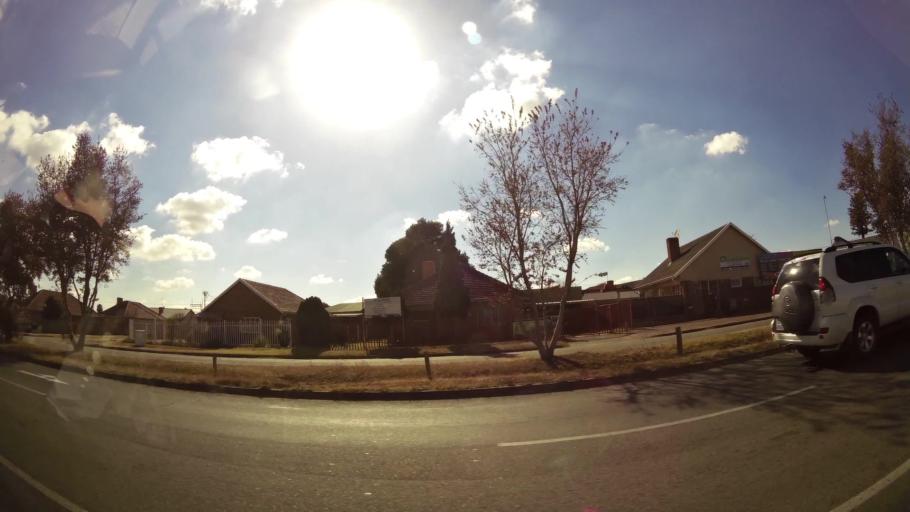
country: ZA
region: Gauteng
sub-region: City of Johannesburg Metropolitan Municipality
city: Roodepoort
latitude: -26.1293
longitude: 27.8331
